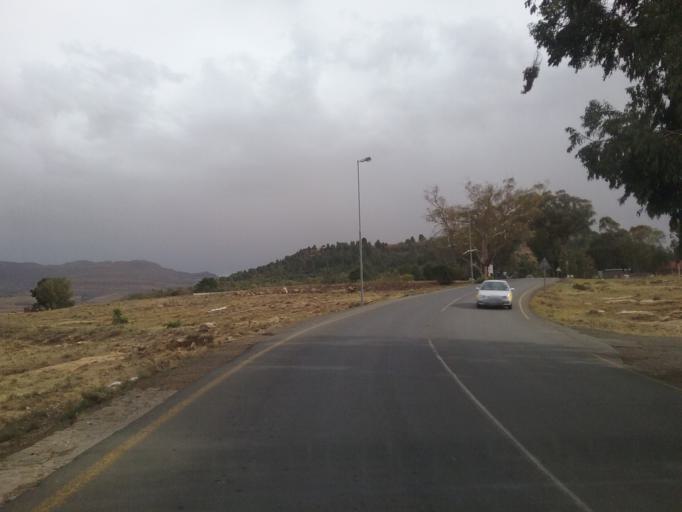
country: LS
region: Quthing
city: Quthing
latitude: -30.4039
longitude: 27.7091
